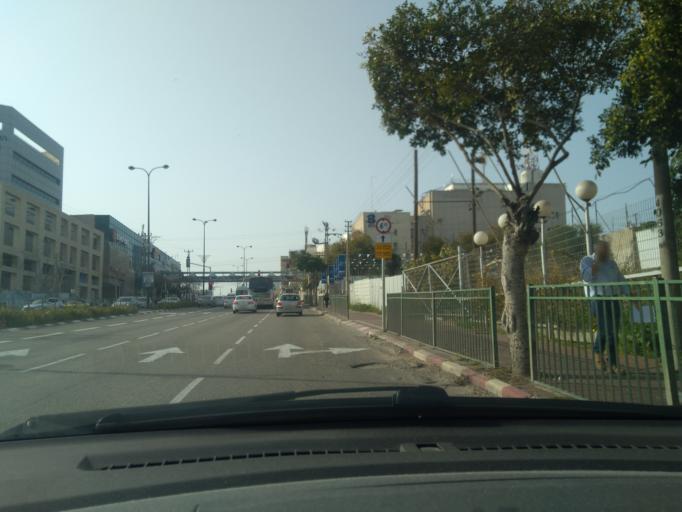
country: IL
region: Central District
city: Netanya
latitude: 32.3263
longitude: 34.8637
